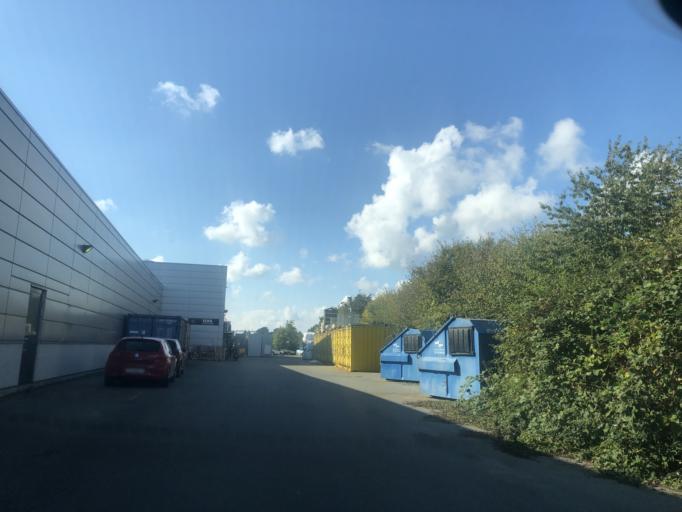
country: DK
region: Capital Region
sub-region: Tarnby Kommune
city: Tarnby
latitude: 55.6173
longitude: 12.6119
